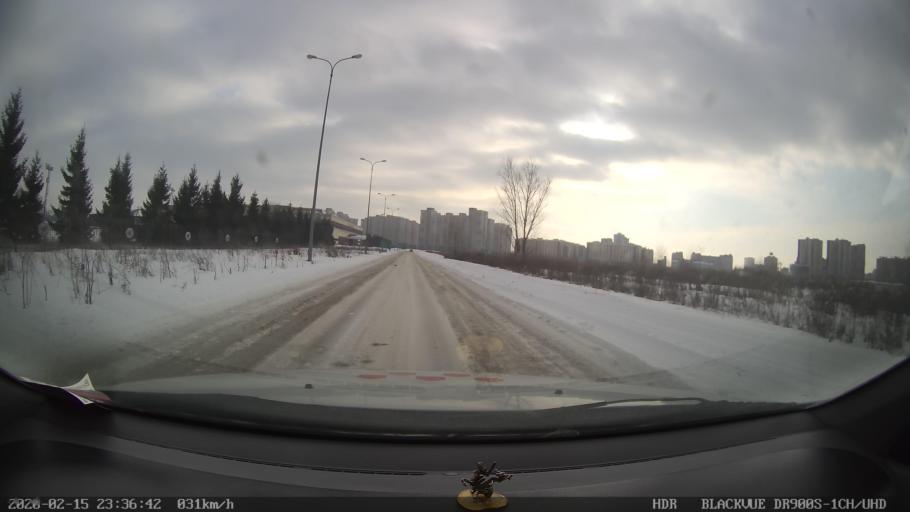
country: RU
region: Tatarstan
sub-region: Gorod Kazan'
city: Kazan
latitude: 55.7920
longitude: 49.1930
